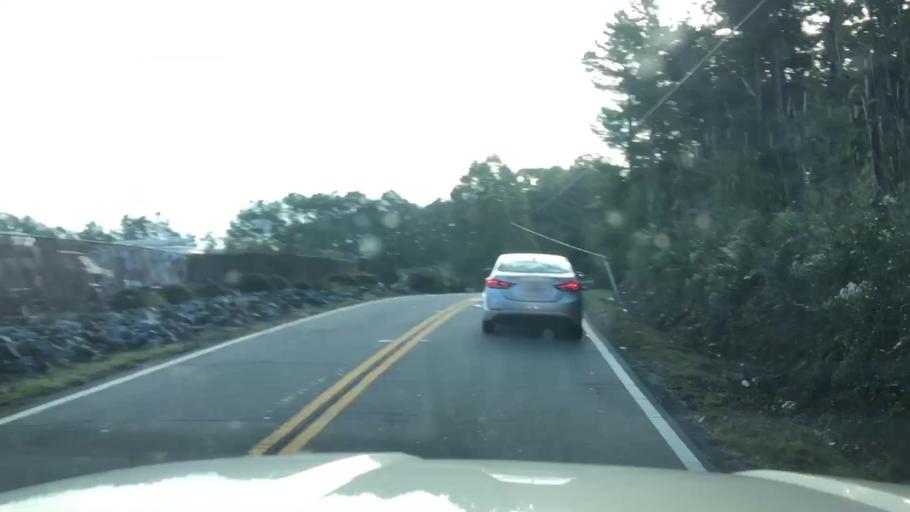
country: US
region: Georgia
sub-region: Bartow County
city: Emerson
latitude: 34.0791
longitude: -84.7316
